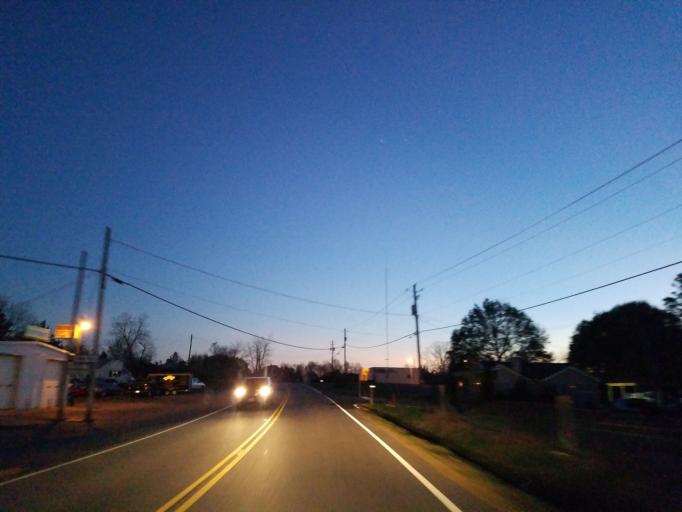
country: US
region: Georgia
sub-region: Dawson County
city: Dawsonville
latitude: 34.3182
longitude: -84.1075
